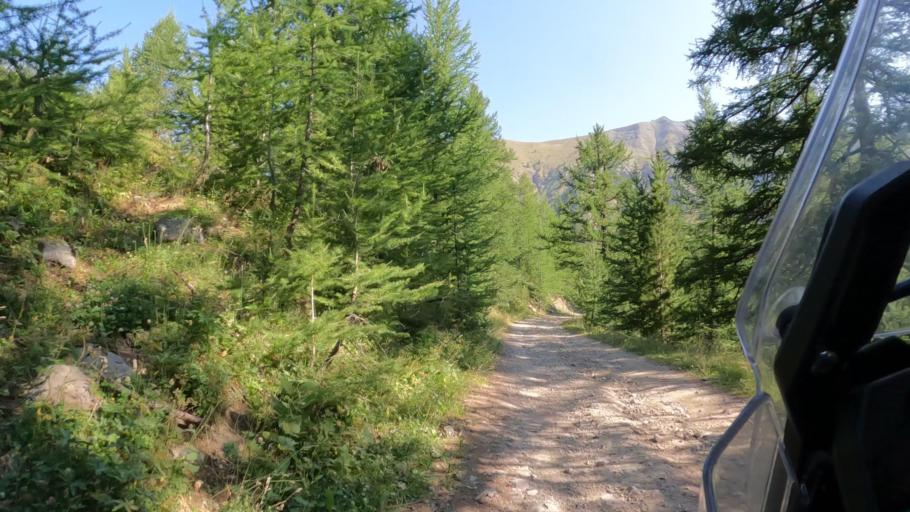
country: FR
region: Provence-Alpes-Cote d'Azur
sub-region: Departement des Hautes-Alpes
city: Guillestre
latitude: 44.5871
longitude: 6.6196
